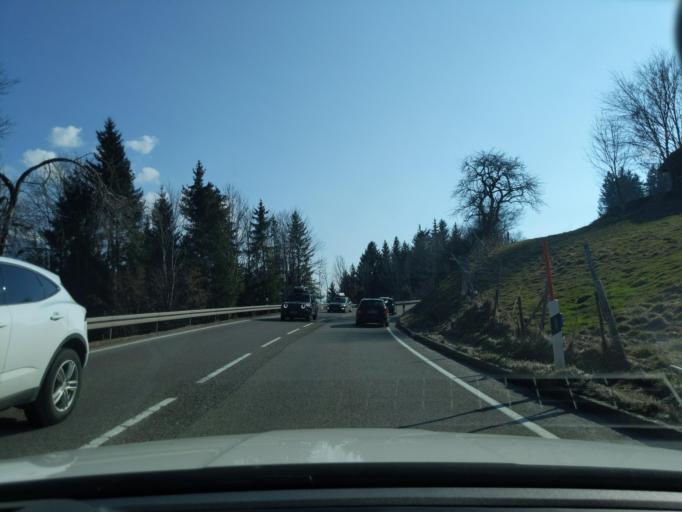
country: DE
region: Bavaria
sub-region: Swabia
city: Sonthofen
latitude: 47.4867
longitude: 10.2671
